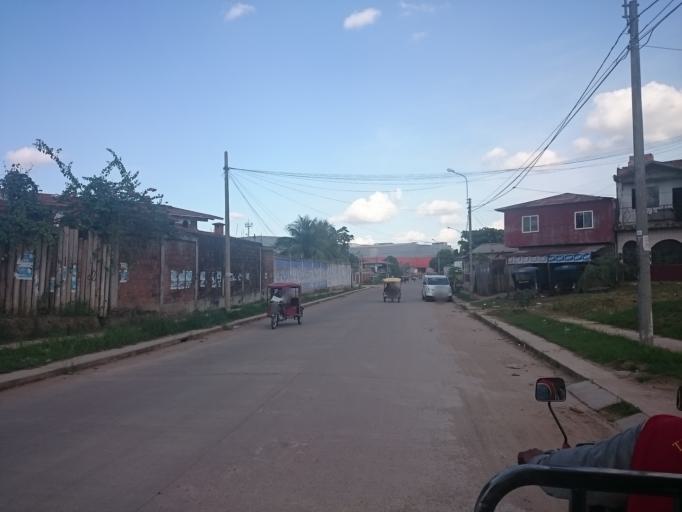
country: PE
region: Ucayali
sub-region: Provincia de Coronel Portillo
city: Pucallpa
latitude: -8.3825
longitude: -74.5595
